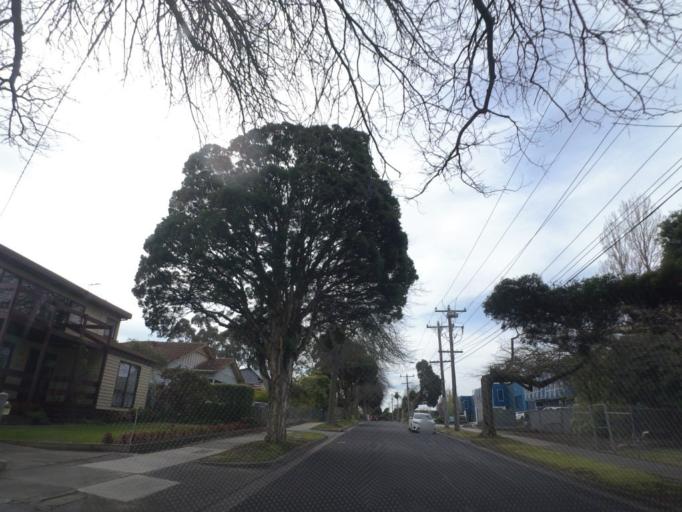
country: AU
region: Victoria
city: Mitcham
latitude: -37.8147
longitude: 145.2021
